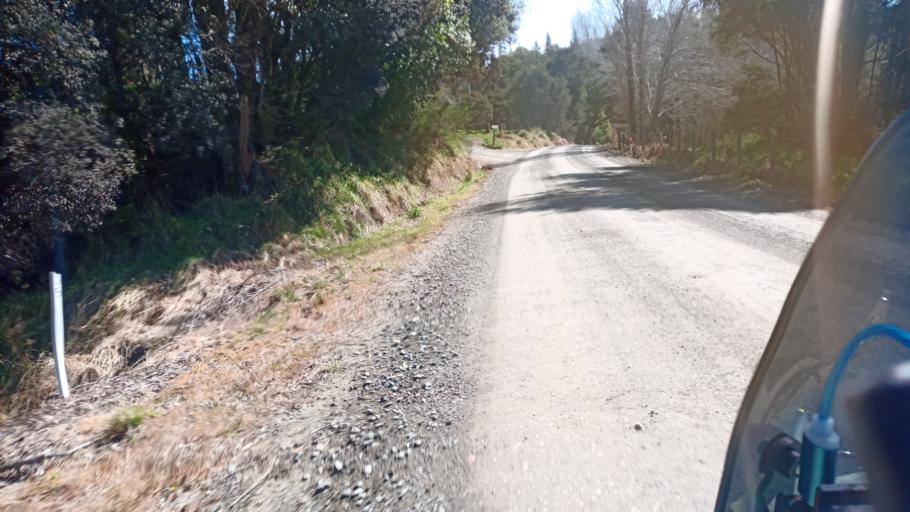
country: NZ
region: Gisborne
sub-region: Gisborne District
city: Gisborne
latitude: -37.9958
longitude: 178.3111
